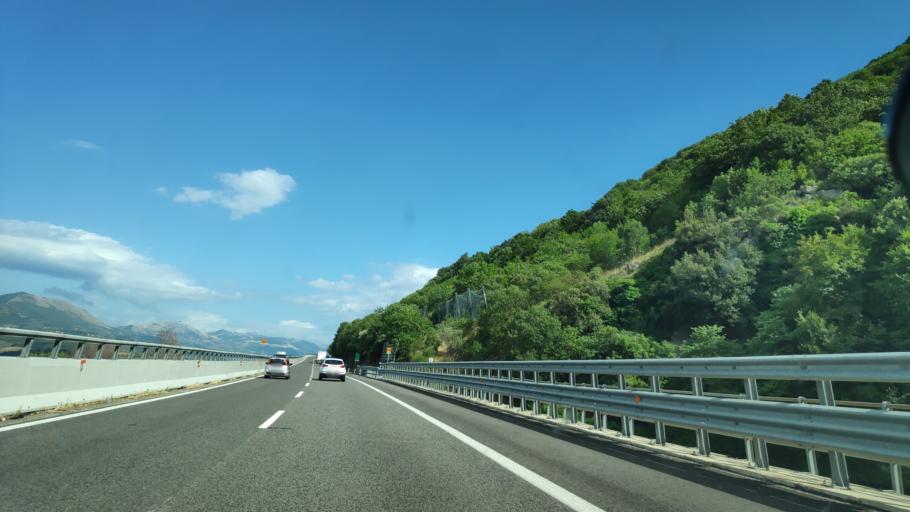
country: IT
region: Campania
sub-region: Provincia di Salerno
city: Sicignano degli Alburni
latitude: 40.5920
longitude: 15.3264
